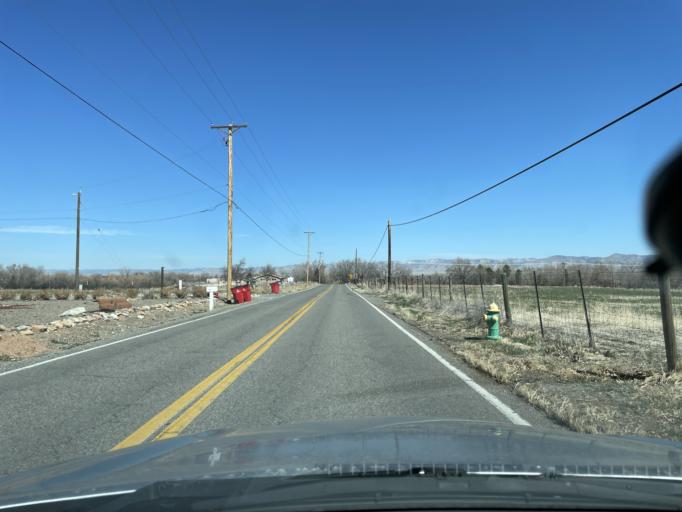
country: US
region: Colorado
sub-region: Mesa County
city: Redlands
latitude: 39.0864
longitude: -108.6687
